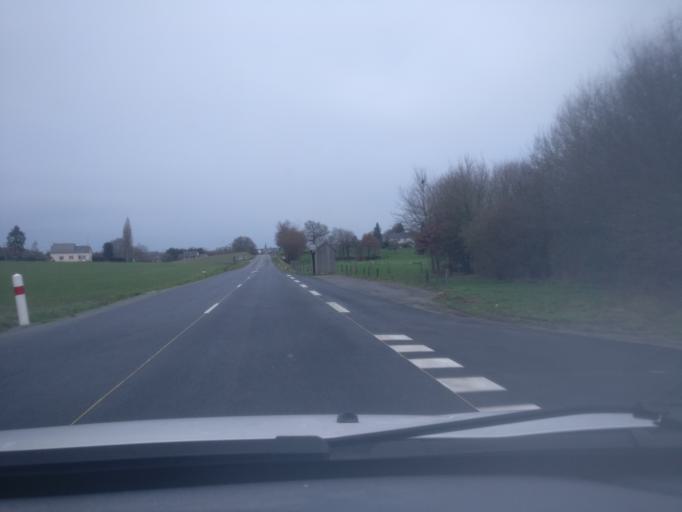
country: FR
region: Brittany
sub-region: Departement d'Ille-et-Vilaine
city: Bais
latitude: 47.9969
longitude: -1.2874
